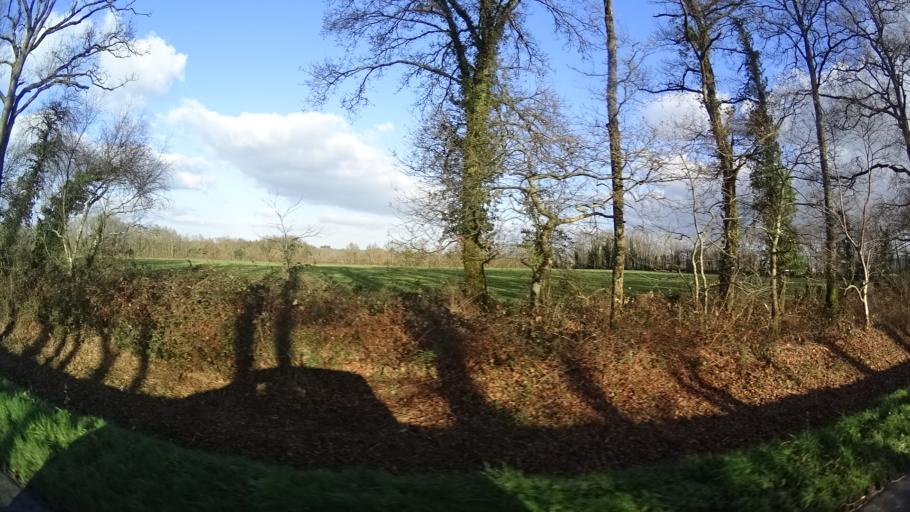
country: FR
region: Pays de la Loire
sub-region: Departement de la Loire-Atlantique
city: Plesse
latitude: 47.5259
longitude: -1.8996
